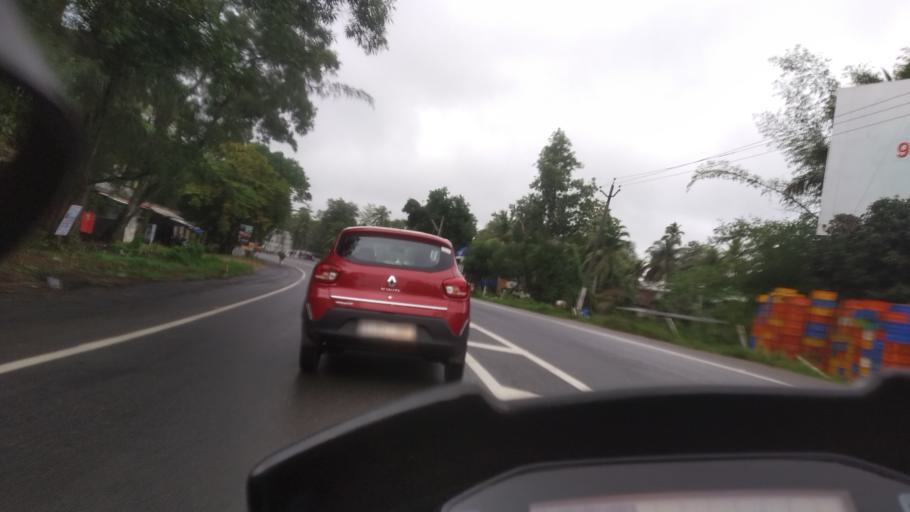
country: IN
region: Kerala
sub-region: Alappuzha
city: Mavelikara
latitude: 9.3185
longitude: 76.4260
